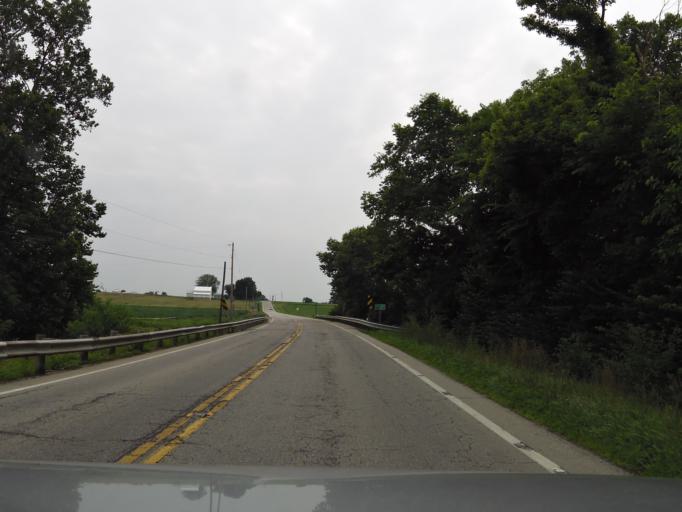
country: US
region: Ohio
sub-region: Clinton County
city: Blanchester
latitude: 39.3461
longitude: -83.8893
